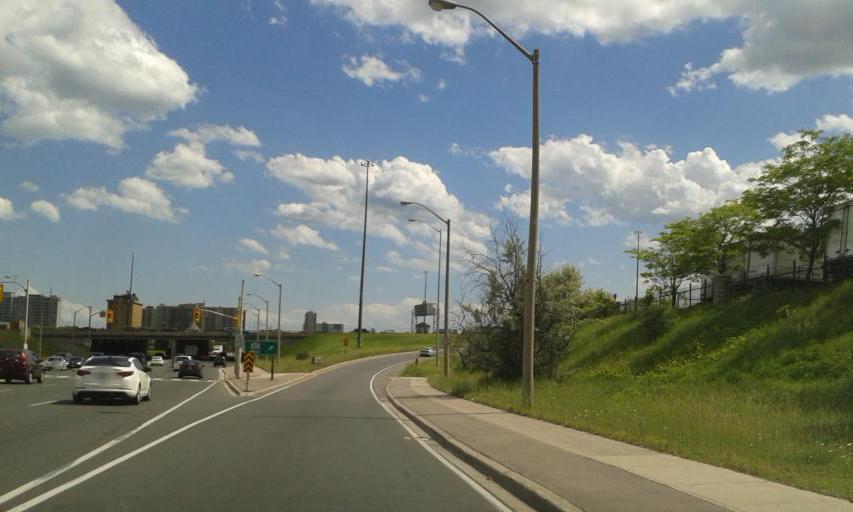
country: CA
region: Ontario
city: Scarborough
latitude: 43.7879
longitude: -79.2365
